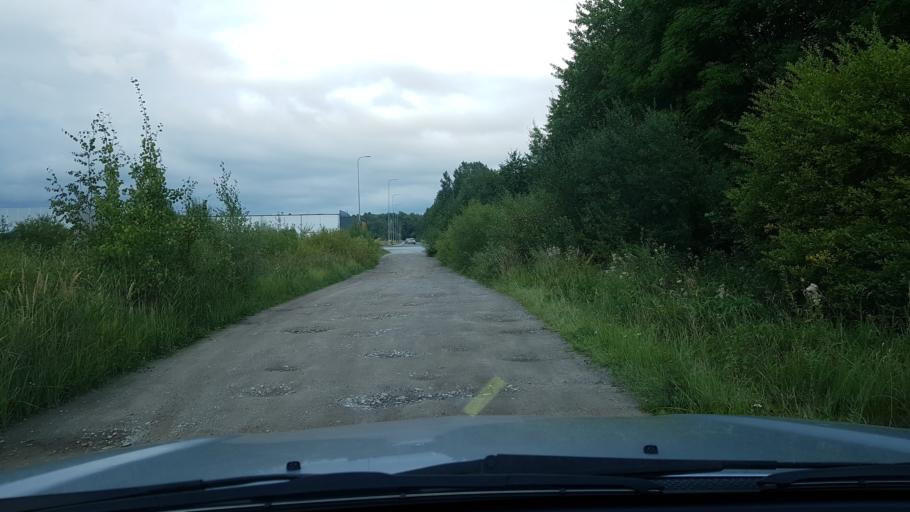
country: EE
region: Harju
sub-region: Rae vald
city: Jueri
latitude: 59.3933
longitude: 24.8279
